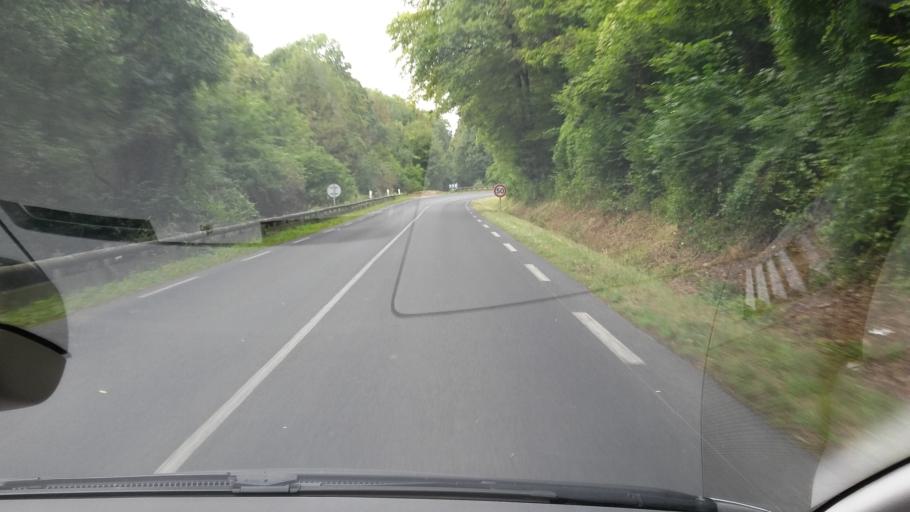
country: FR
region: Champagne-Ardenne
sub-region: Departement de la Marne
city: Verzenay
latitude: 49.1323
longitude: 4.1041
